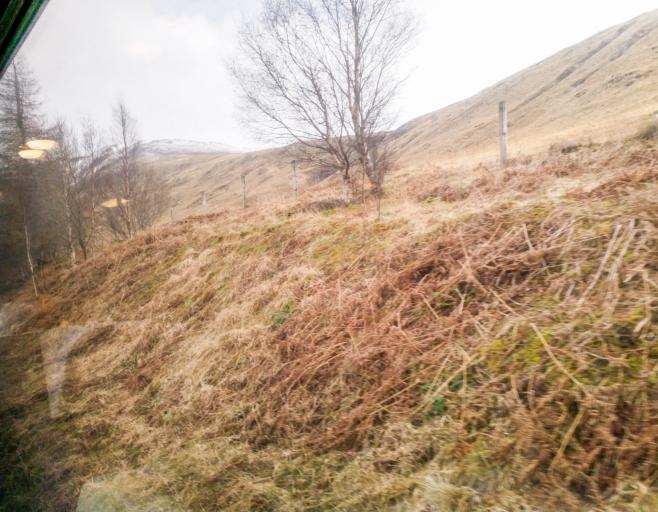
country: GB
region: Scotland
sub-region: Highland
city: Spean Bridge
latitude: 56.8107
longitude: -4.7176
